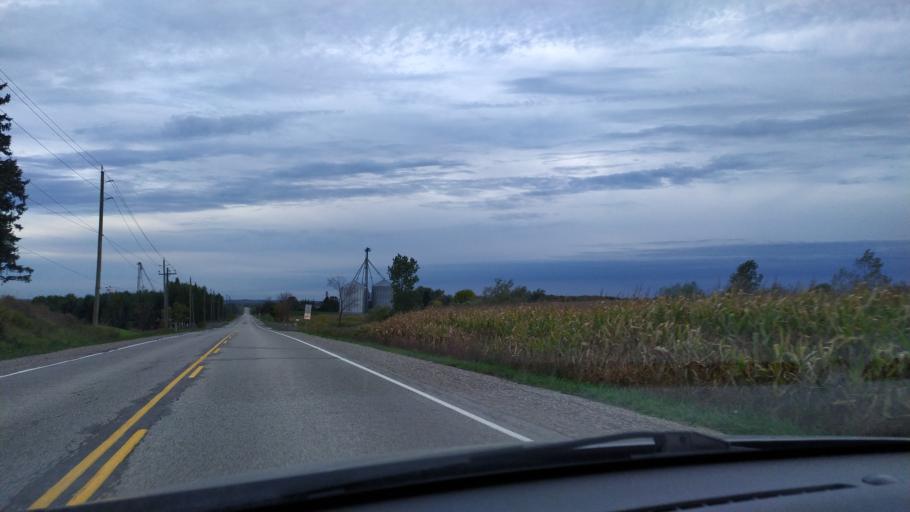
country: CA
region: Ontario
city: Stratford
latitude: 43.5014
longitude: -80.7639
